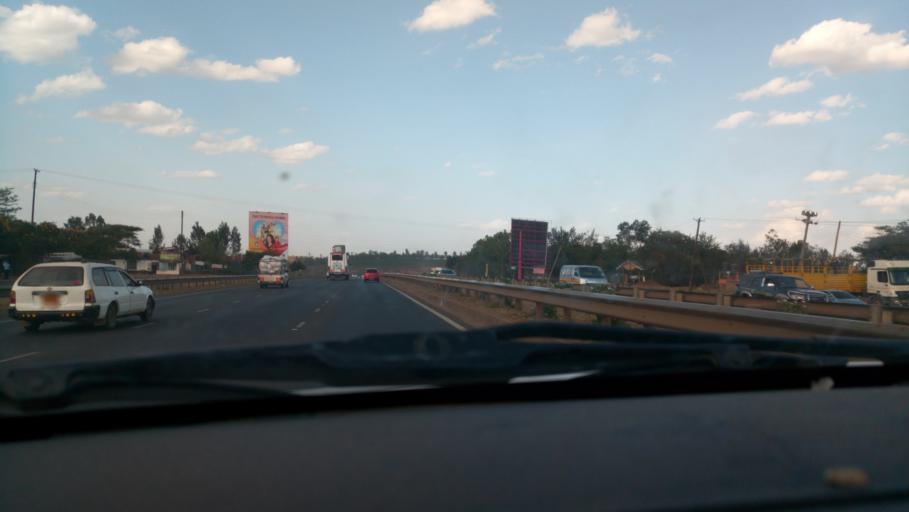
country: KE
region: Nairobi Area
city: Thika
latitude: -1.0937
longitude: 37.0305
